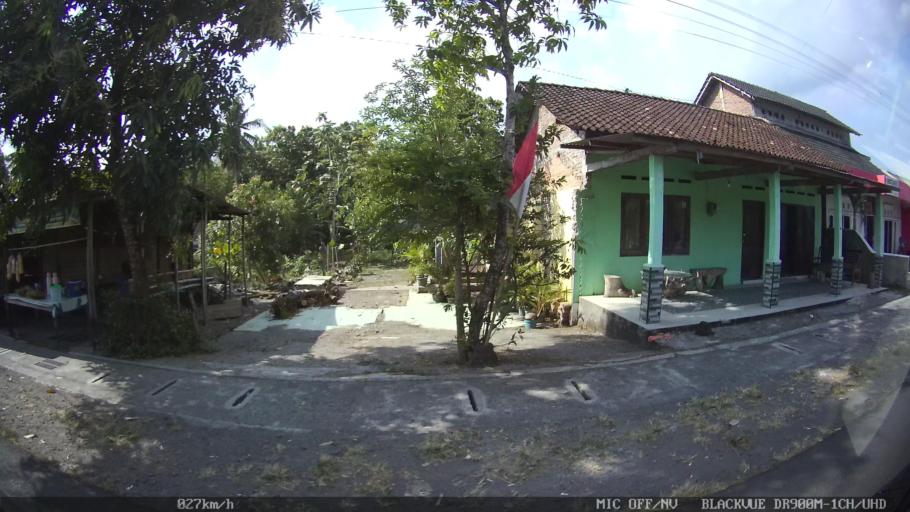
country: ID
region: Daerah Istimewa Yogyakarta
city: Kasihan
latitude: -7.8377
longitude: 110.3165
